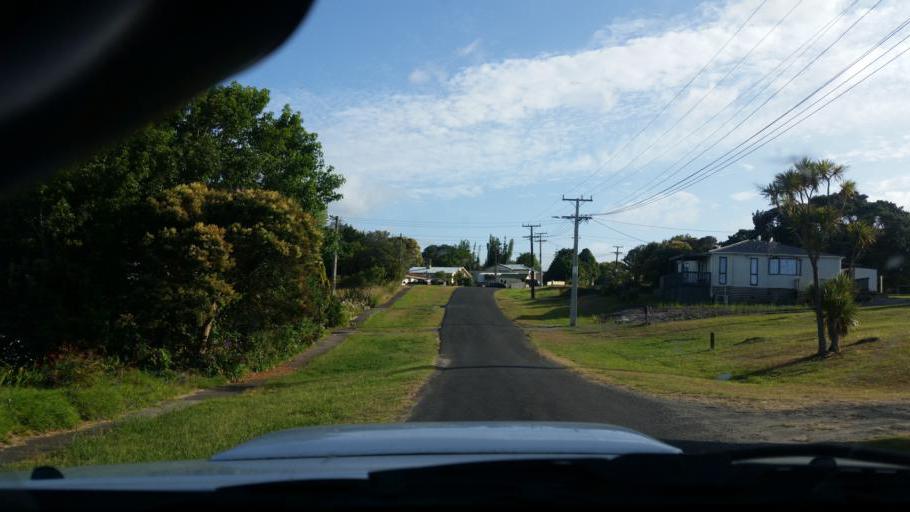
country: NZ
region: Northland
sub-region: Kaipara District
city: Dargaville
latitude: -35.9357
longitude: 173.8586
